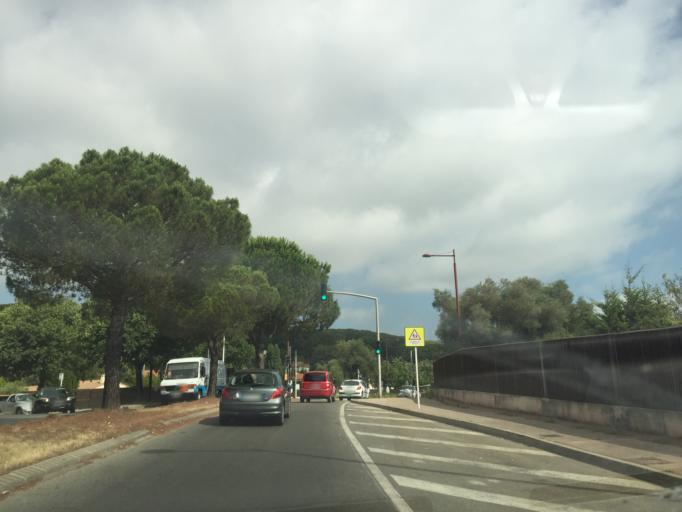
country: FR
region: Provence-Alpes-Cote d'Azur
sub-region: Departement des Alpes-Maritimes
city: Vallauris
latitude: 43.5793
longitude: 7.0901
